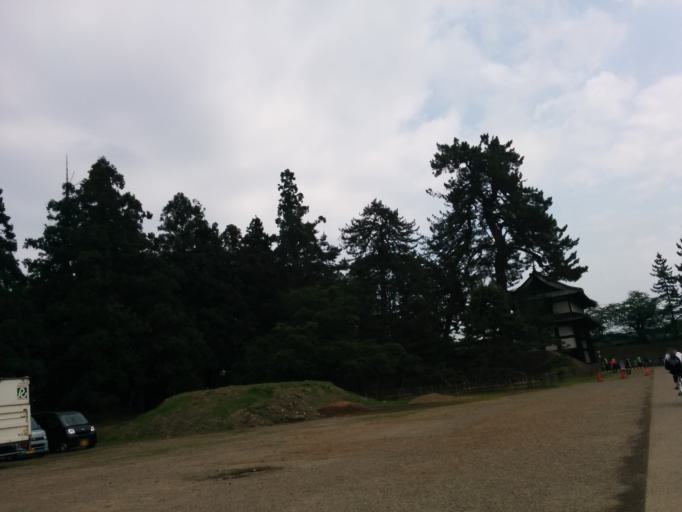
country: JP
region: Aomori
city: Hirosaki
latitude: 40.6110
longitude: 140.4667
